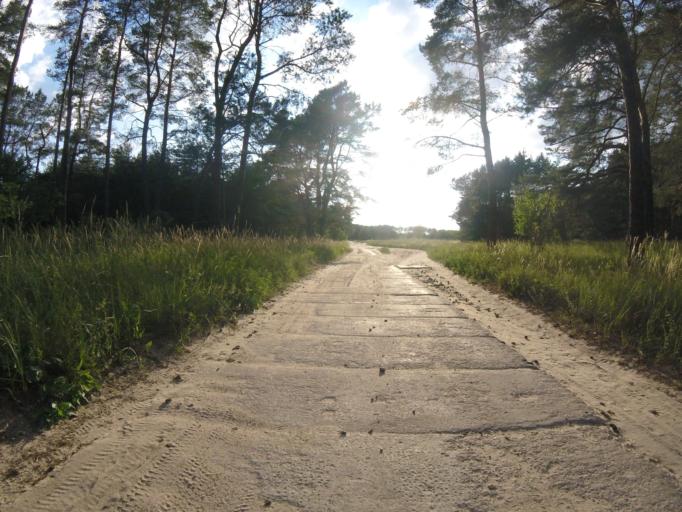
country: DE
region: Brandenburg
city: Schwerin
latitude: 52.1963
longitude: 13.6128
